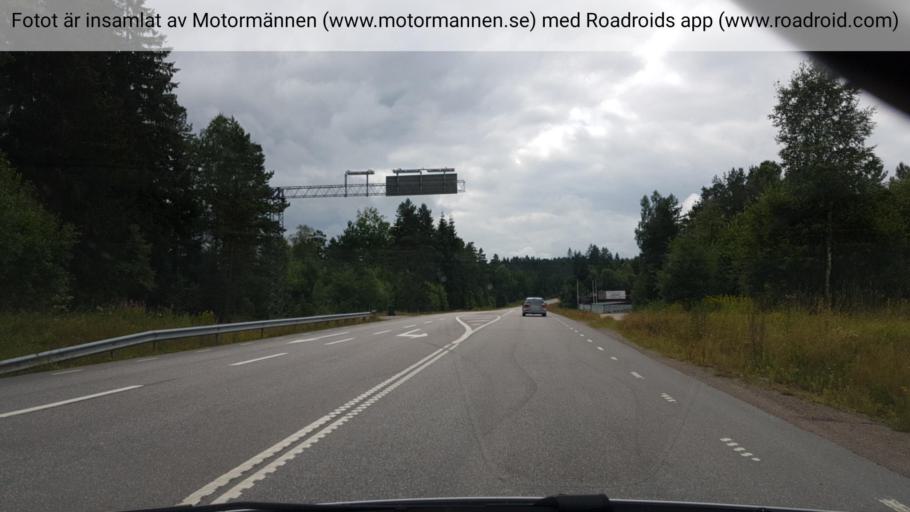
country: SE
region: Vaestra Goetaland
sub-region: Boras Kommun
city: Dalsjofors
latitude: 57.7635
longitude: 13.1145
